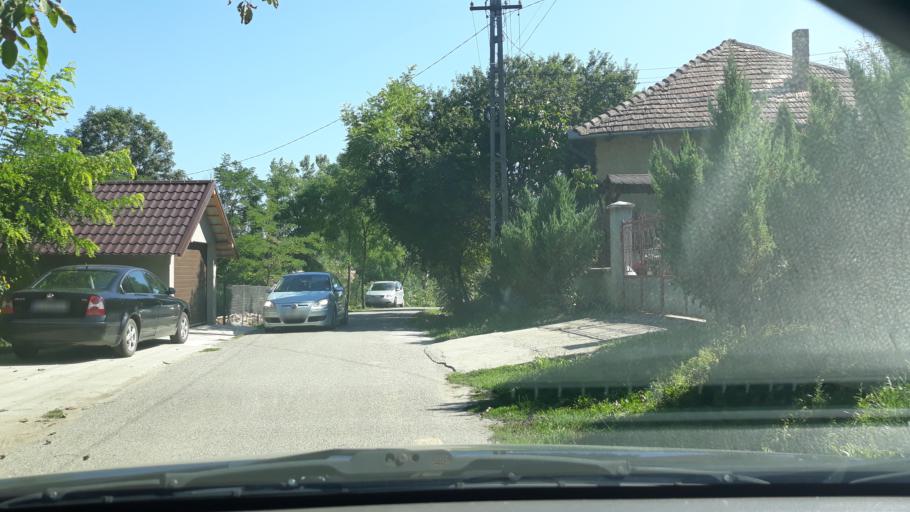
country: RO
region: Salaj
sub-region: Comuna Dobrin
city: Dobrin
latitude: 47.2939
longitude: 23.0928
